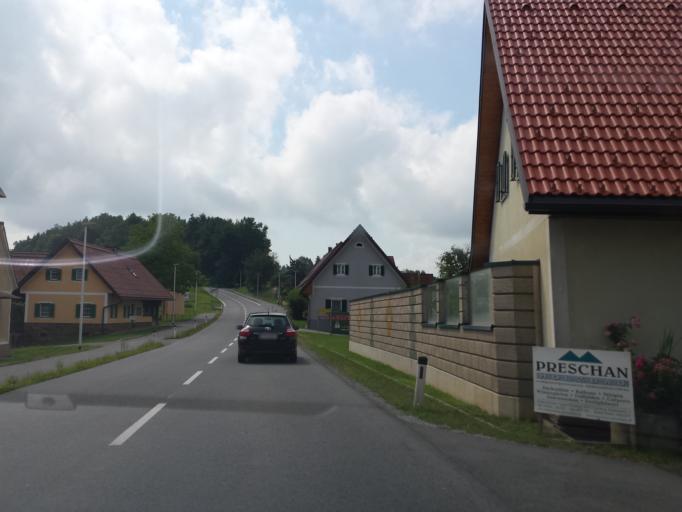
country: AT
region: Styria
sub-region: Politischer Bezirk Deutschlandsberg
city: Stainz
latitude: 46.8782
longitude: 15.2592
